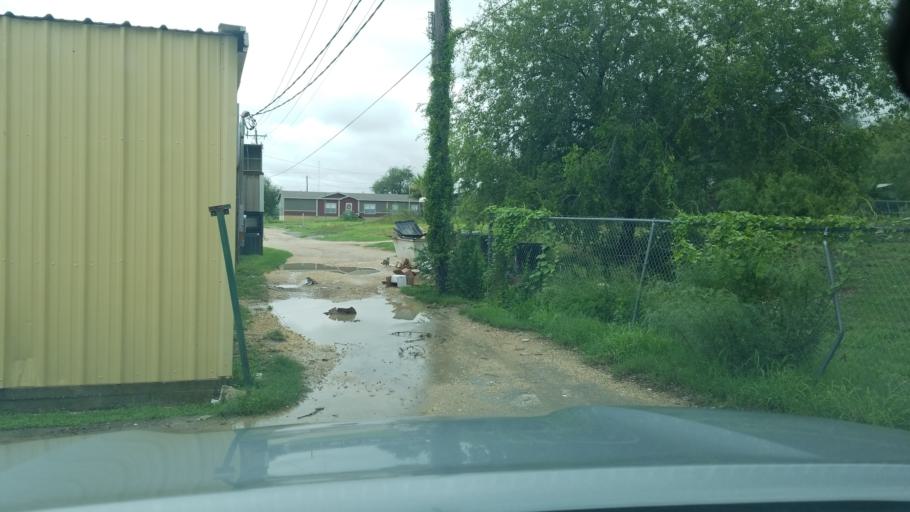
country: US
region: Texas
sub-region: Dimmit County
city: Carrizo Springs
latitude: 28.5255
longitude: -99.8561
